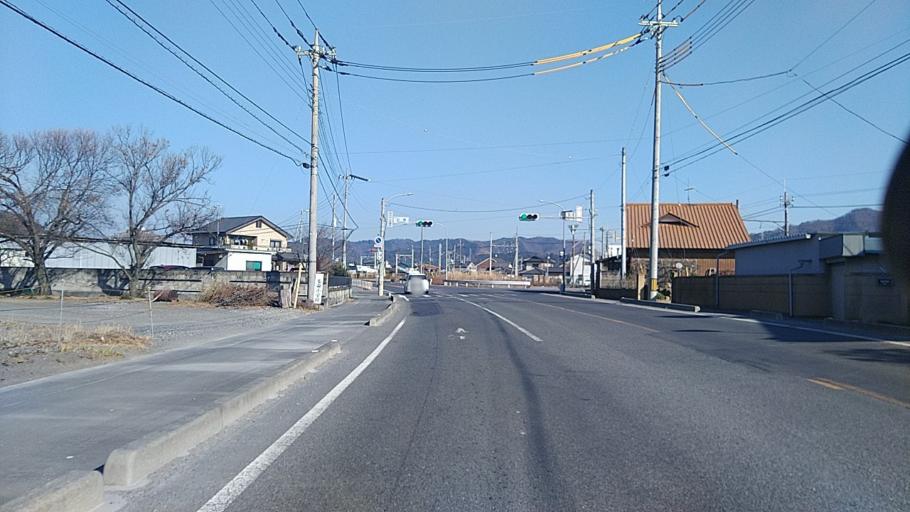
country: JP
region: Tochigi
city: Tanuma
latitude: 36.3735
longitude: 139.5887
